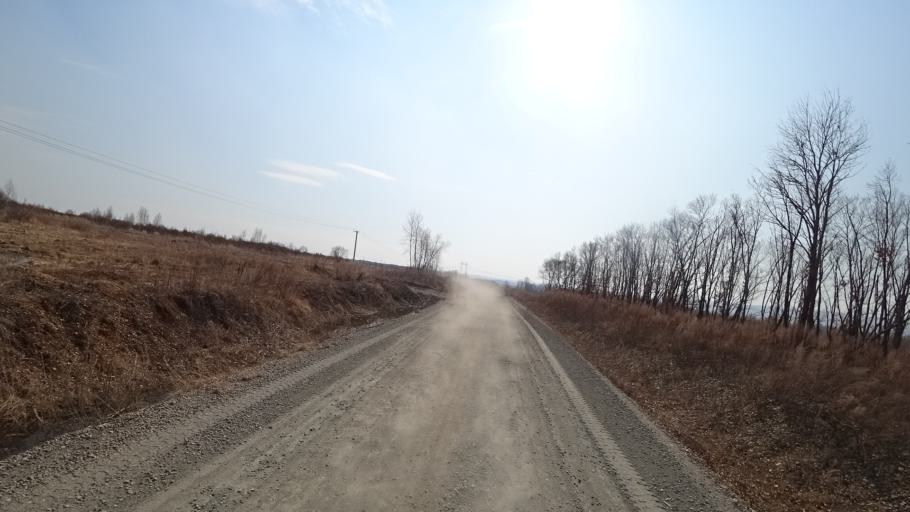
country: RU
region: Amur
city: Novobureyskiy
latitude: 49.8190
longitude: 129.9801
